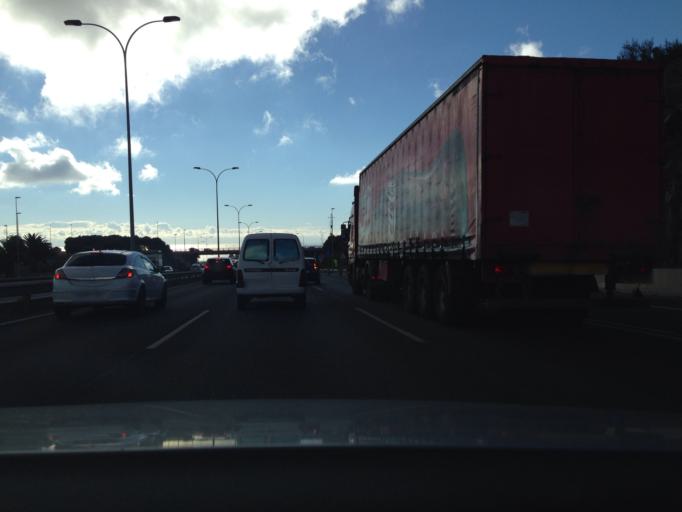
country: ES
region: Canary Islands
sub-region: Provincia de Santa Cruz de Tenerife
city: La Laguna
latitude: 28.4778
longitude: -16.3155
